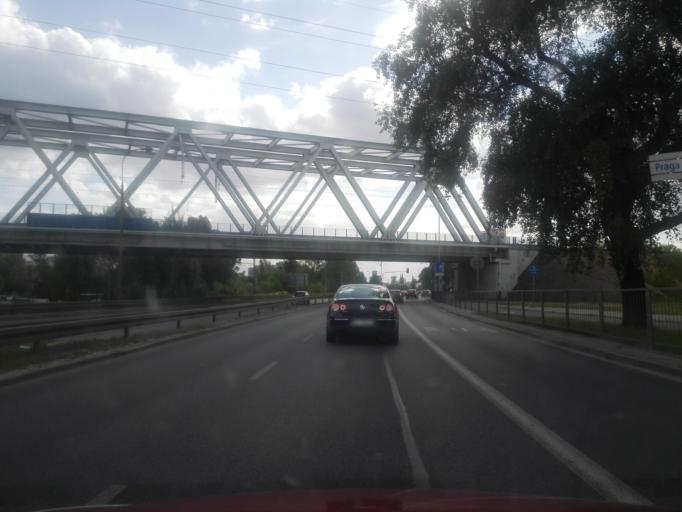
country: PL
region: Masovian Voivodeship
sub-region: Warszawa
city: Praga Polnoc
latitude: 52.2639
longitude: 21.0556
